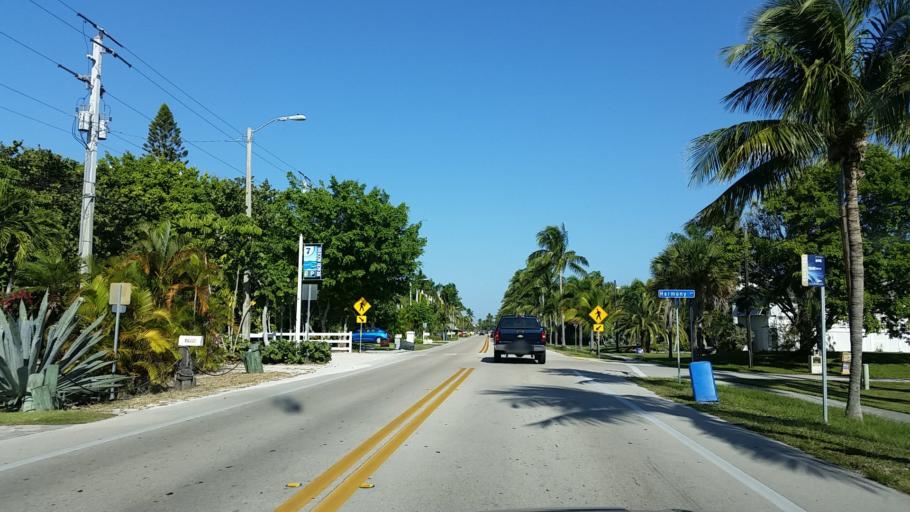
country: US
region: Florida
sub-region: Lee County
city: Bonita Springs
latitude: 26.3504
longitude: -81.8538
